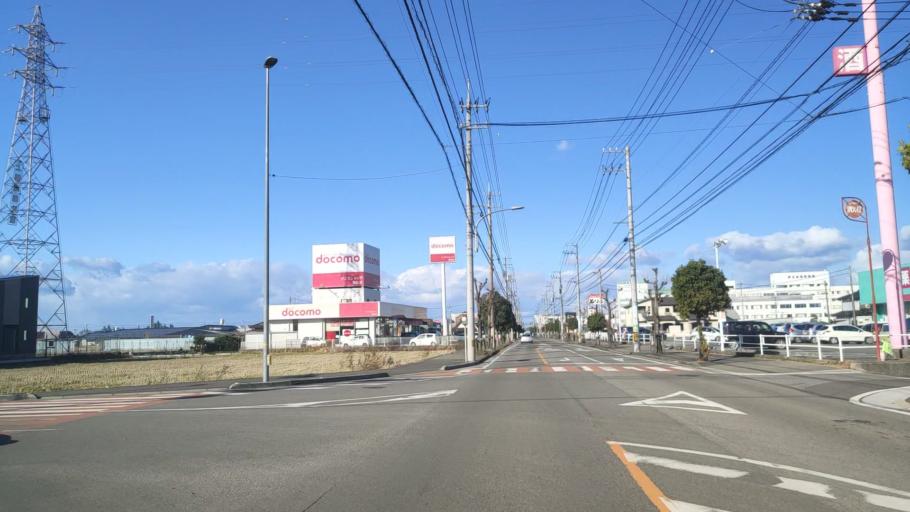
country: JP
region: Ehime
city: Saijo
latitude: 33.9254
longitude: 133.1909
